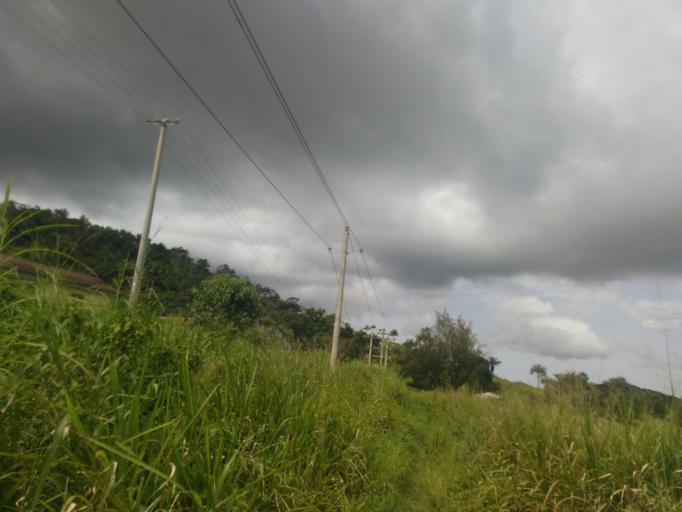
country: SL
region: Northern Province
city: Makali
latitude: 8.6306
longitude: -11.6591
